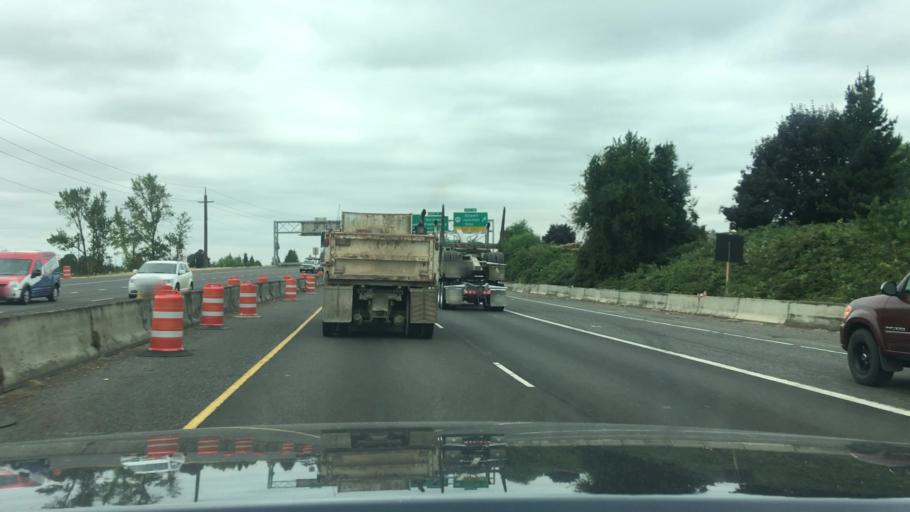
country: US
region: Oregon
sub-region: Lane County
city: Eugene
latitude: 44.0921
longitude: -123.1709
